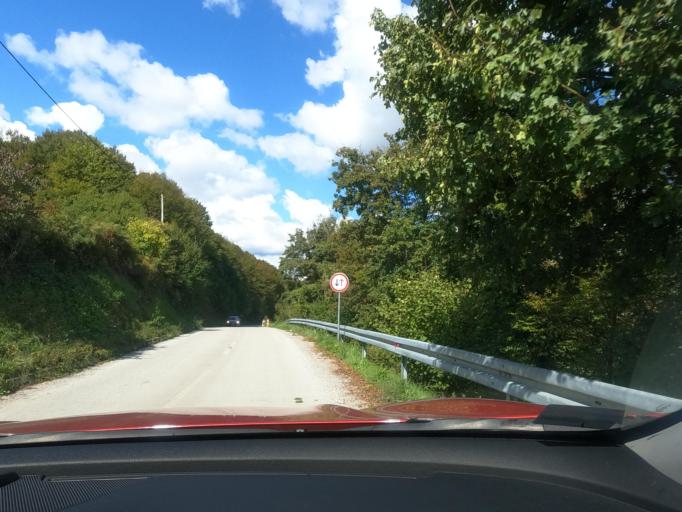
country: BA
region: Federation of Bosnia and Herzegovina
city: Velika Kladusa
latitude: 45.2062
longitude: 15.8073
